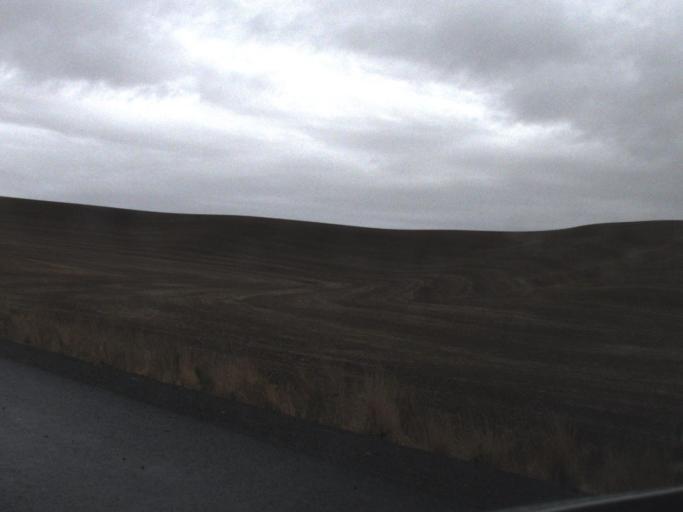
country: US
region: Washington
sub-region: Whitman County
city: Pullman
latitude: 46.7599
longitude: -117.2620
